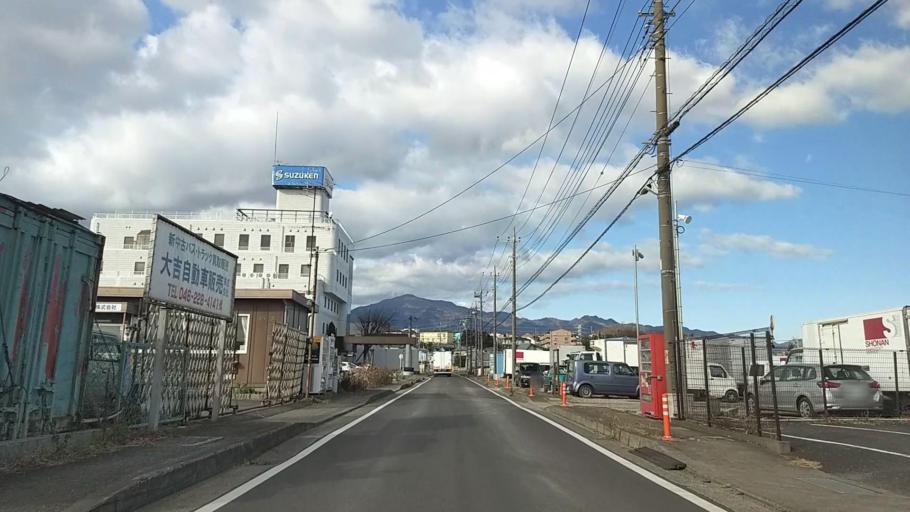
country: JP
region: Kanagawa
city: Atsugi
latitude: 35.4189
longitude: 139.3507
